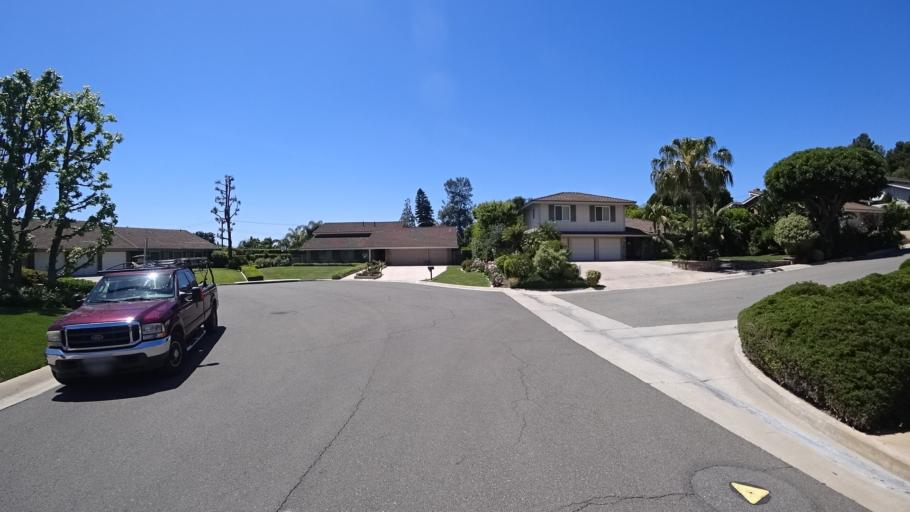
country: US
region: California
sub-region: Orange County
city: Villa Park
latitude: 33.8238
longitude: -117.8172
